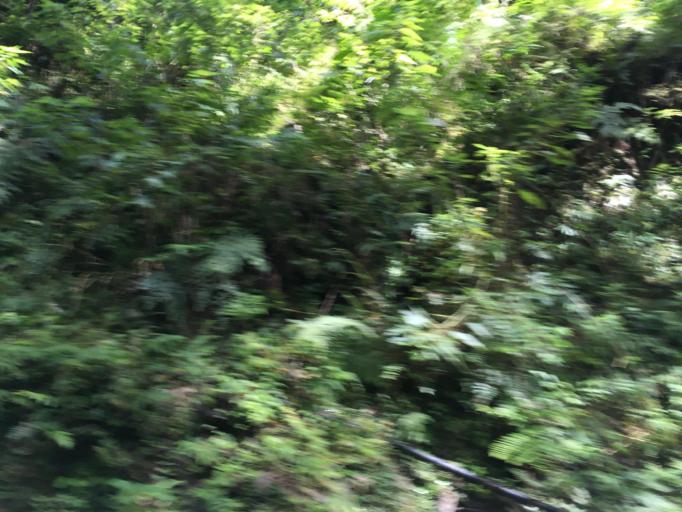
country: TW
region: Taiwan
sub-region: Yilan
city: Yilan
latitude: 24.6177
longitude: 121.4829
